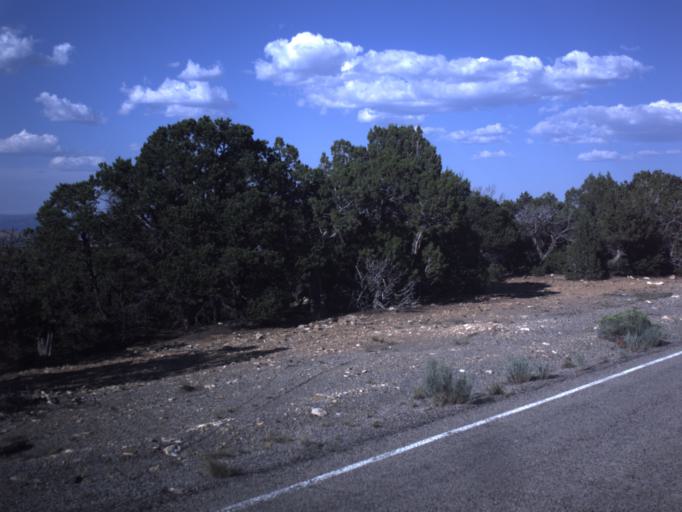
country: US
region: Utah
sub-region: Emery County
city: Huntington
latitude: 39.4861
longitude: -110.9572
